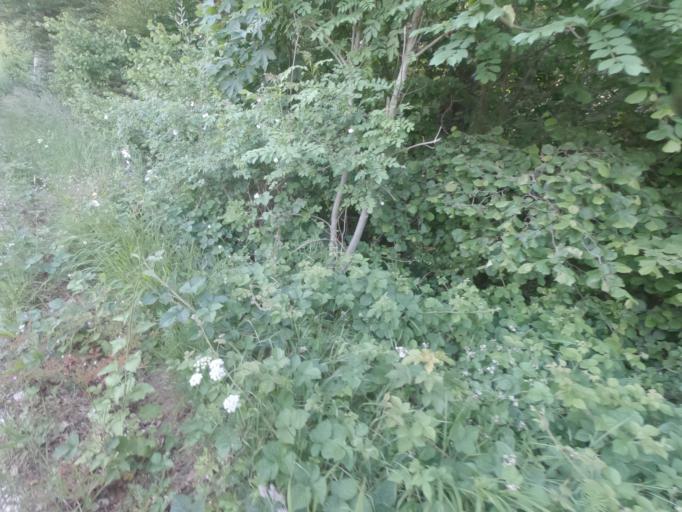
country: CH
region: Solothurn
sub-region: Bezirk Lebern
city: Langendorf
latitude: 47.2415
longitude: 7.5270
